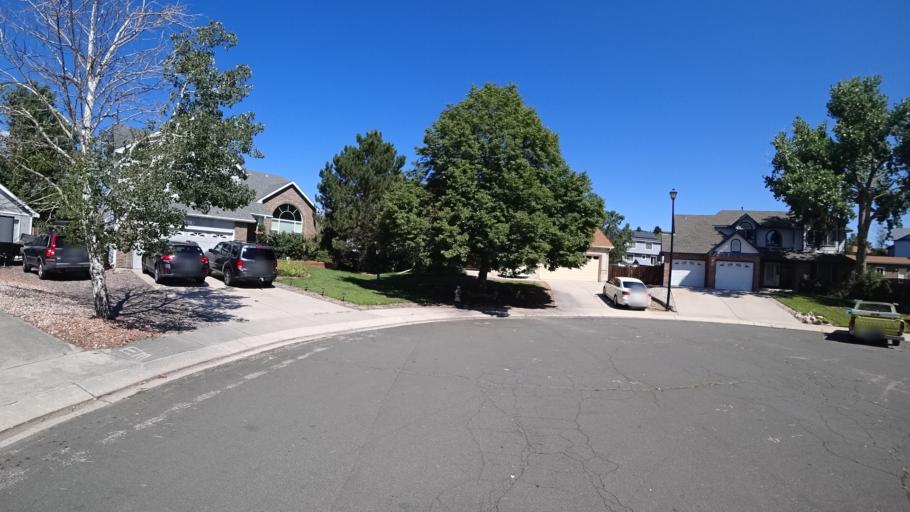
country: US
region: Colorado
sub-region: El Paso County
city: Black Forest
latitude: 38.9430
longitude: -104.7483
